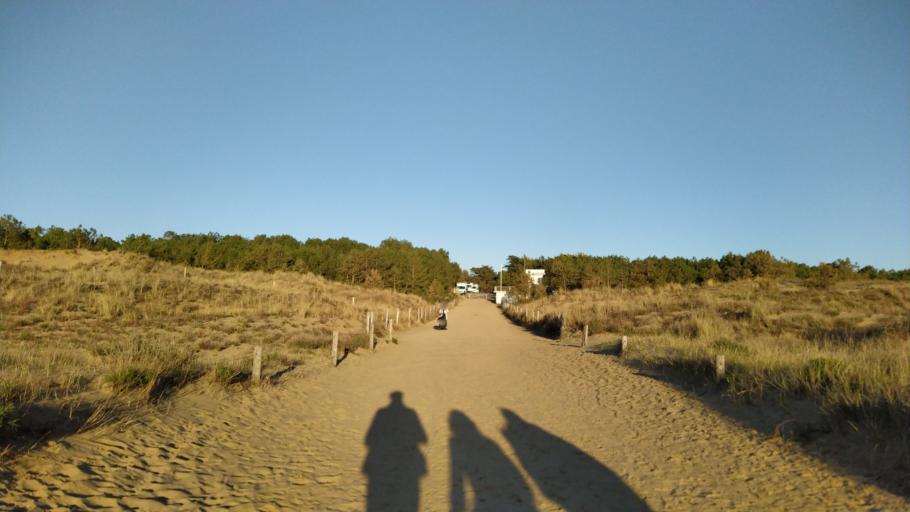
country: FR
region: Pays de la Loire
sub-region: Departement de la Loire-Atlantique
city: Saint-Brevin-les-Pins
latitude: 47.2164
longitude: -2.1652
